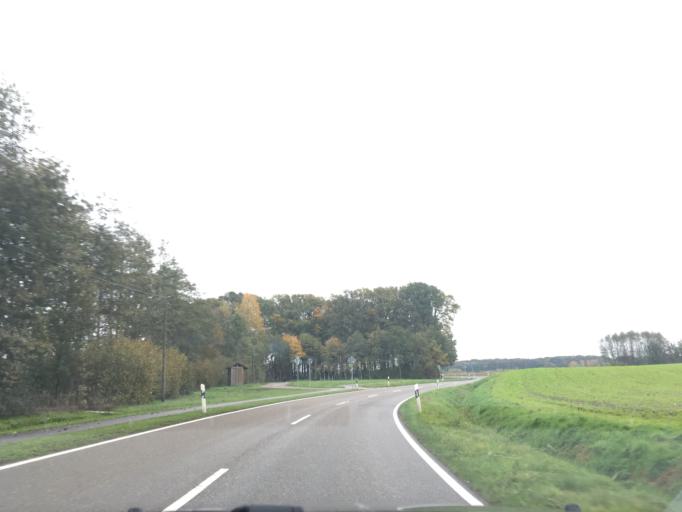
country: DE
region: North Rhine-Westphalia
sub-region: Regierungsbezirk Munster
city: Vreden
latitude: 52.0805
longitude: 6.7666
